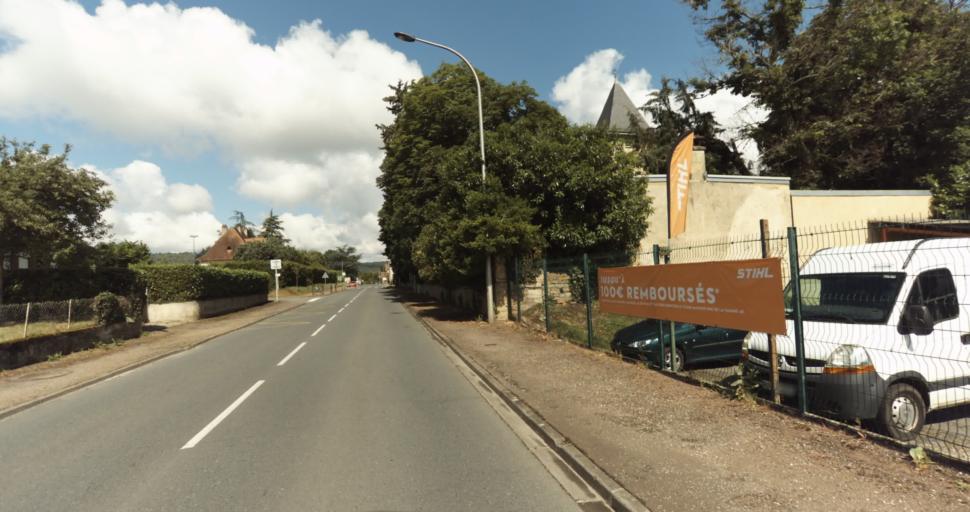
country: FR
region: Aquitaine
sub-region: Departement de la Dordogne
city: Le Bugue
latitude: 44.8460
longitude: 0.9161
